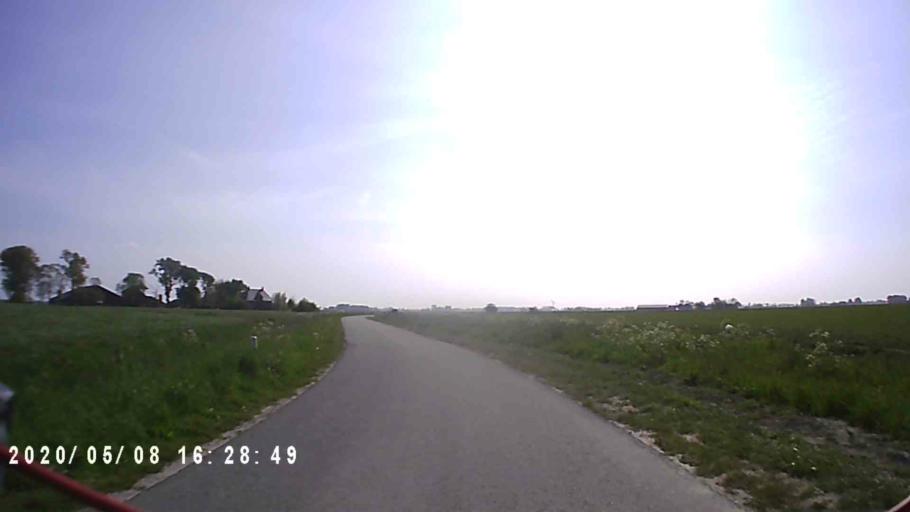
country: NL
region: Groningen
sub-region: Gemeente Bedum
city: Bedum
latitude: 53.3609
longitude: 6.6240
